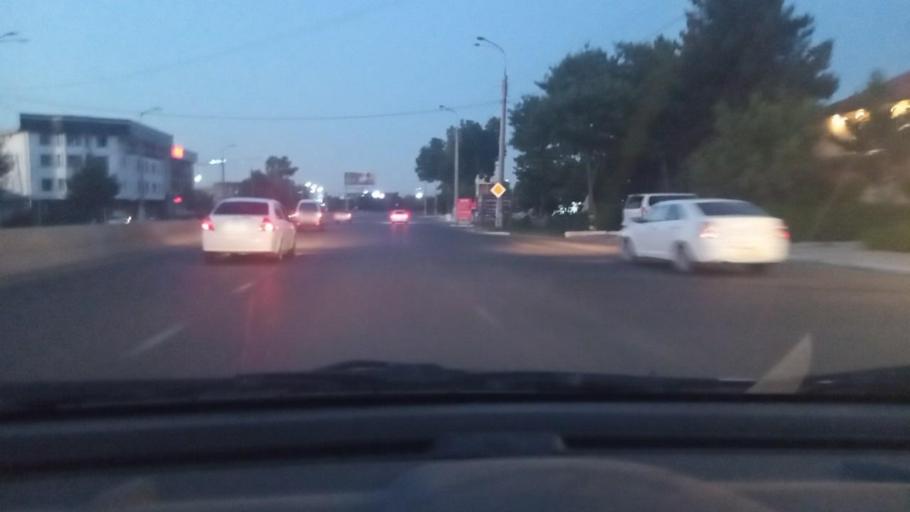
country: UZ
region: Toshkent Shahri
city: Tashkent
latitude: 41.2478
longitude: 69.2180
